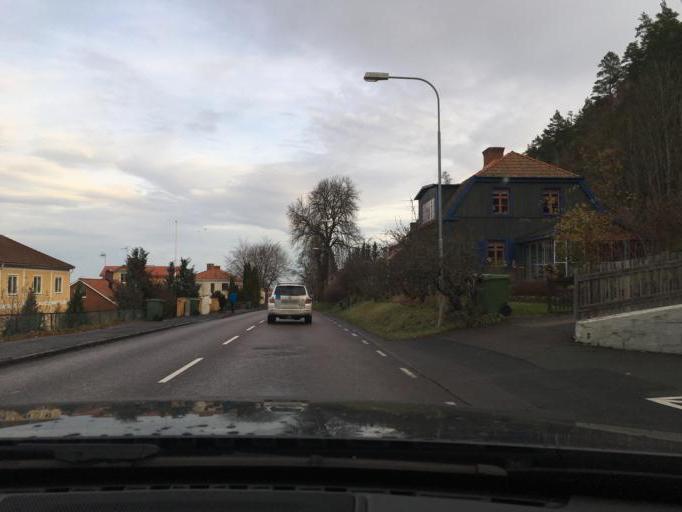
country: SE
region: Joenkoeping
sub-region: Jonkopings Kommun
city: Graenna
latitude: 58.0155
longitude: 14.4602
